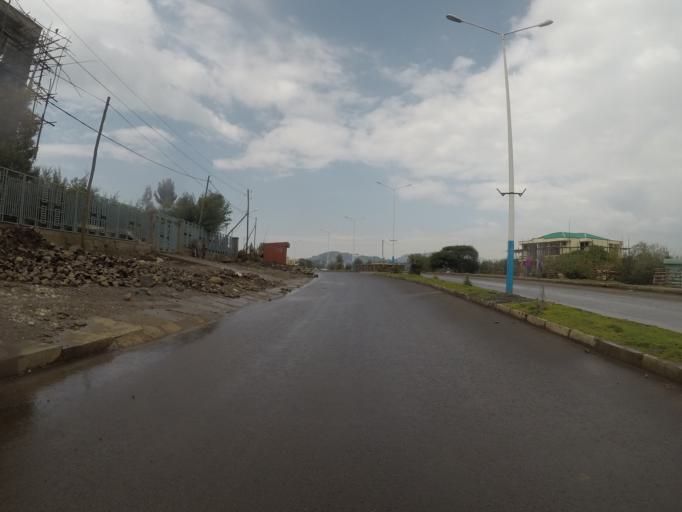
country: ET
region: Amhara
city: Debark'
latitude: 13.1451
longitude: 37.8941
